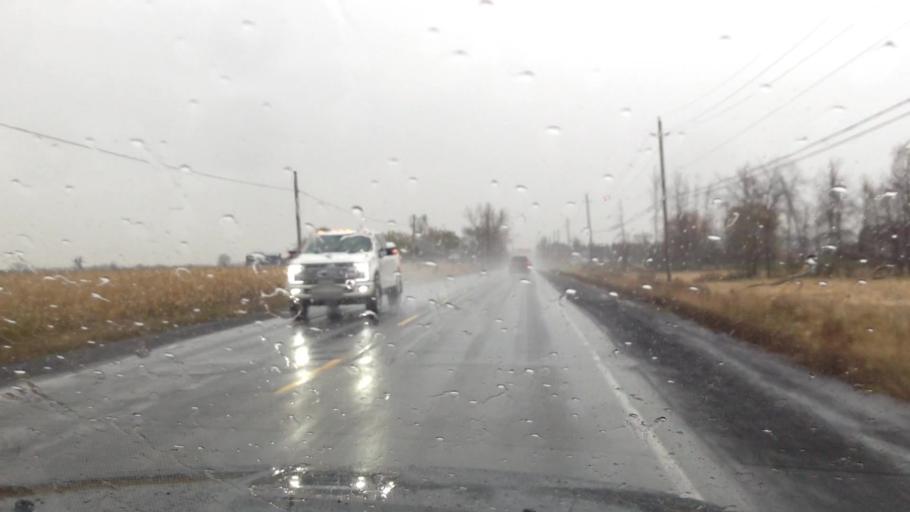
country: CA
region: Ontario
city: Bourget
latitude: 45.2959
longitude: -75.3259
